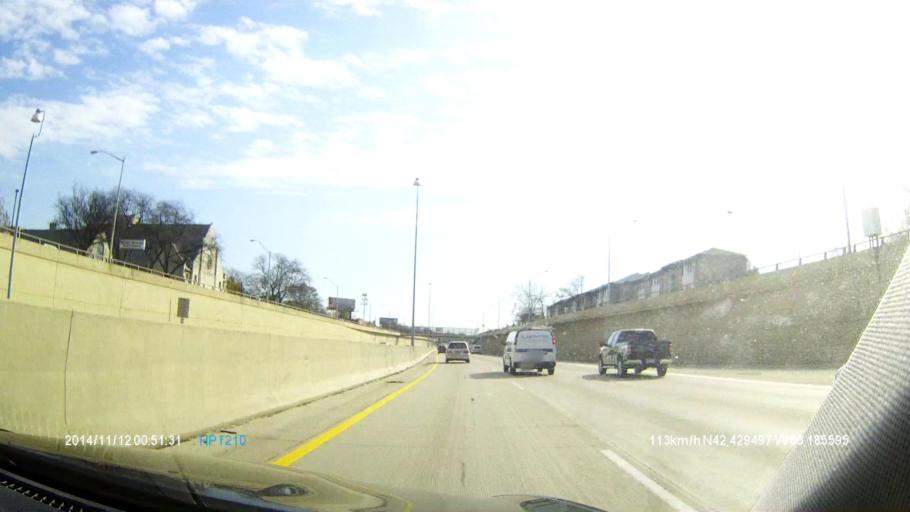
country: US
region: Michigan
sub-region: Oakland County
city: Oak Park
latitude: 42.4292
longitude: -83.1852
